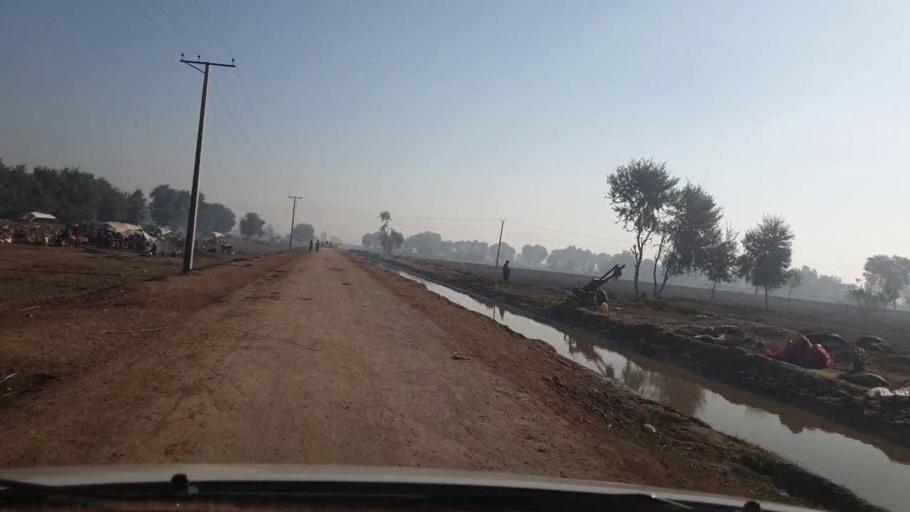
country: PK
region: Sindh
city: Dadu
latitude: 26.6838
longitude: 67.7926
